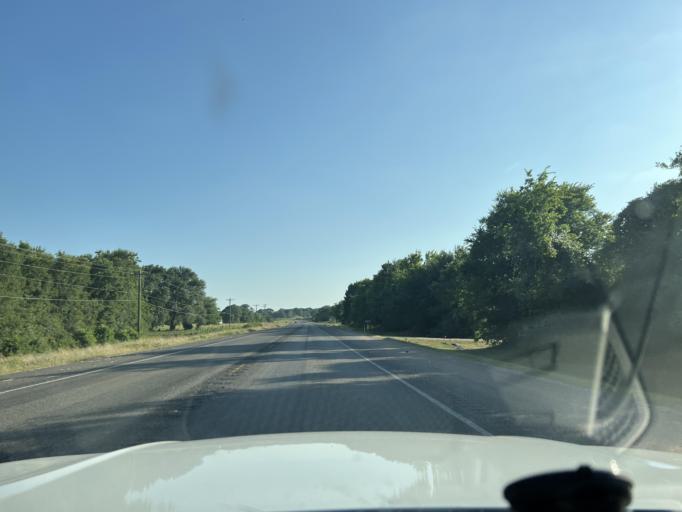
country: US
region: Texas
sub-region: Washington County
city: Brenham
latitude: 30.2247
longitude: -96.2981
